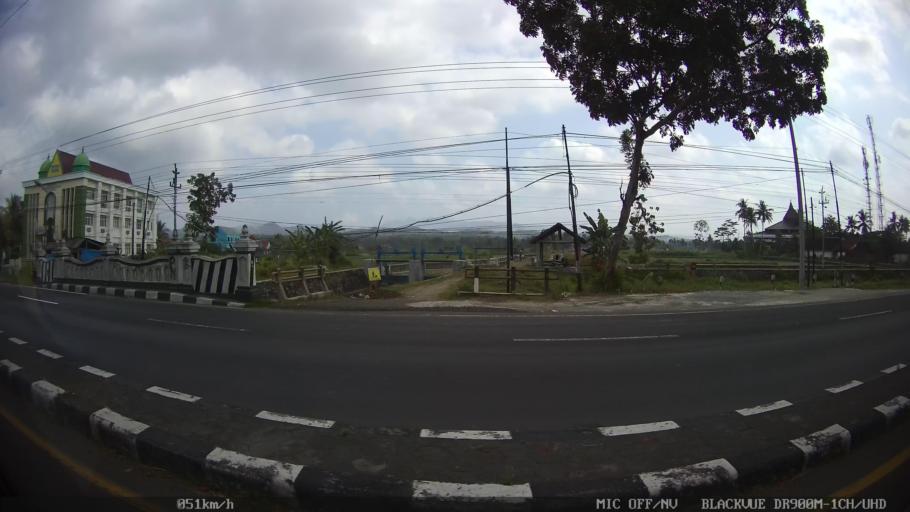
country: ID
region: Daerah Istimewa Yogyakarta
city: Srandakan
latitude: -7.8690
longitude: 110.1474
